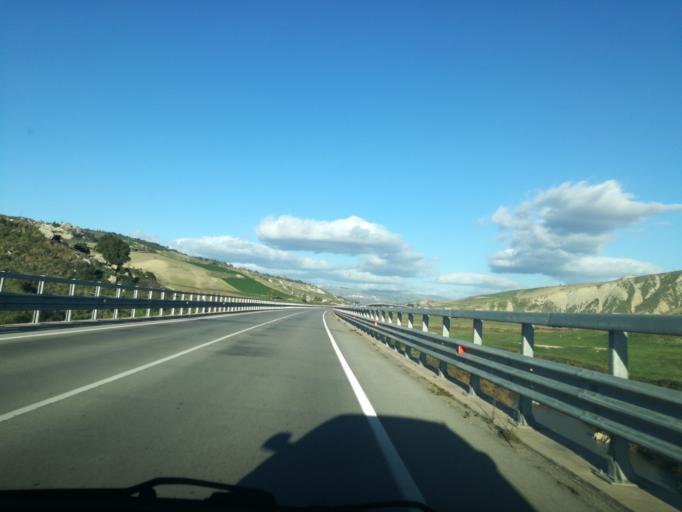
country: IT
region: Sicily
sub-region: Enna
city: Pietraperzia
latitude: 37.4247
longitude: 14.0744
